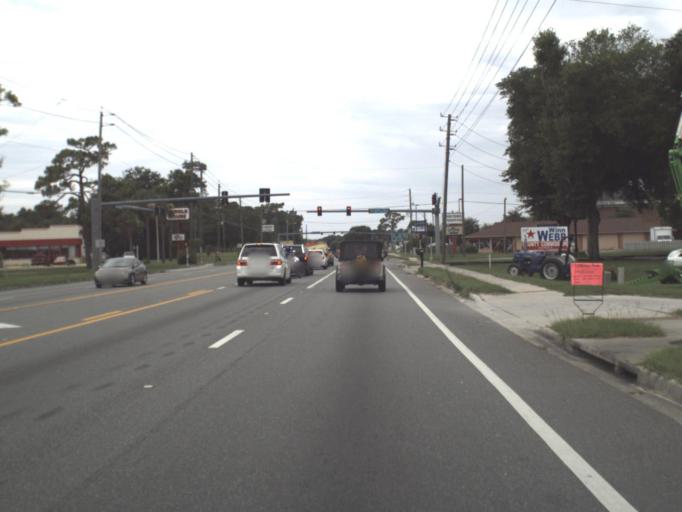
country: US
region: Florida
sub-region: Citrus County
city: Crystal River
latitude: 28.8979
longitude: -82.5690
